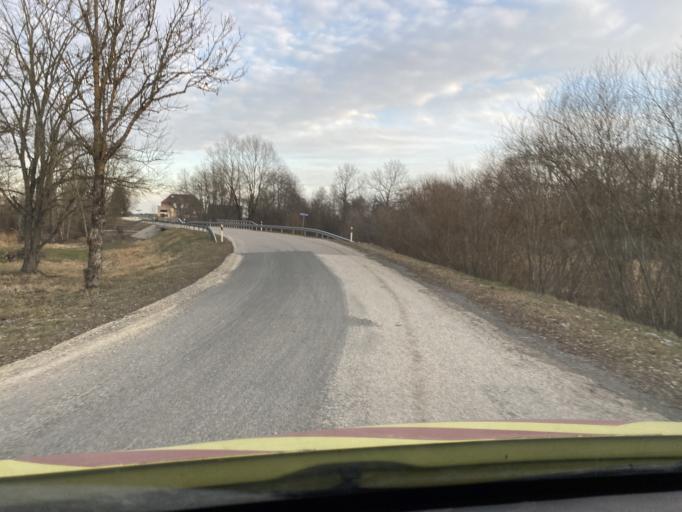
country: EE
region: Jogevamaa
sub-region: Poltsamaa linn
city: Poltsamaa
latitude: 58.5833
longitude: 26.1006
